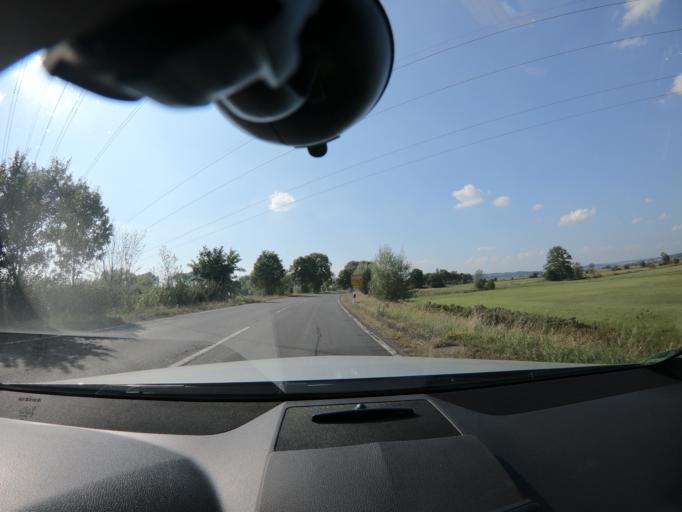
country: DE
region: Hesse
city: Amoneburg
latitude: 50.8031
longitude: 8.8994
